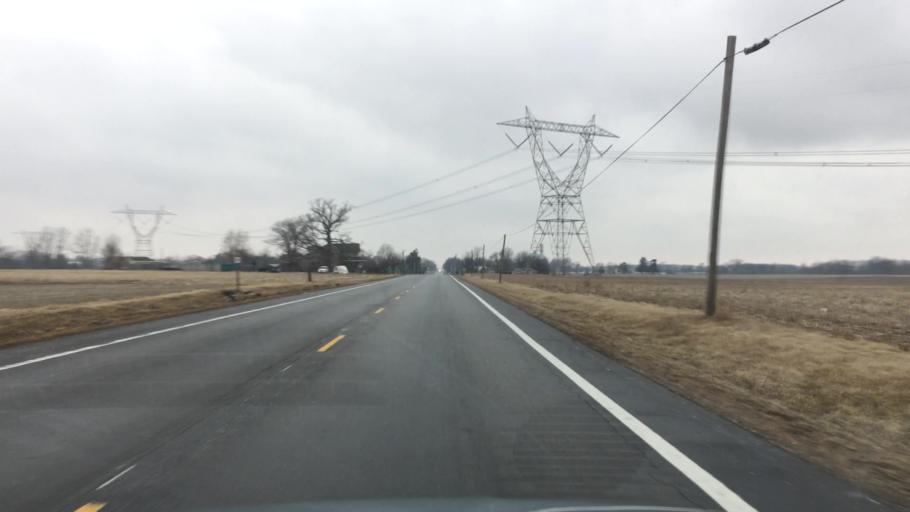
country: US
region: Ohio
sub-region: Mercer County
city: Celina
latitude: 40.5955
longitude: -84.4789
